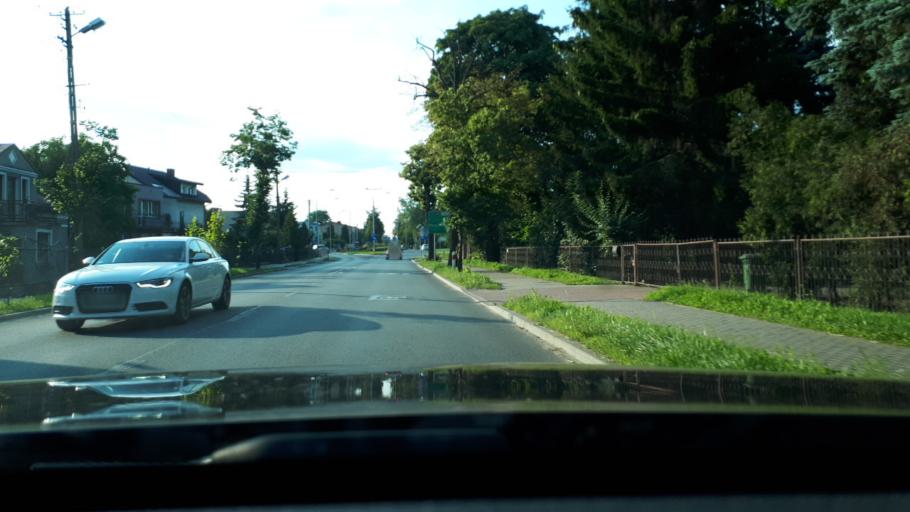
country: PL
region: Masovian Voivodeship
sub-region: Powiat ciechanowski
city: Ciechanow
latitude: 52.8665
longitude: 20.6260
